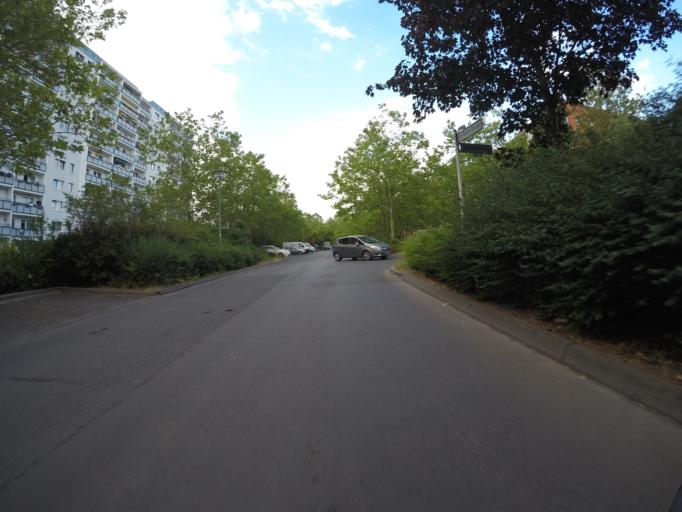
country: DE
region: Berlin
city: Kaulsdorf
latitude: 52.5216
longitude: 13.5932
